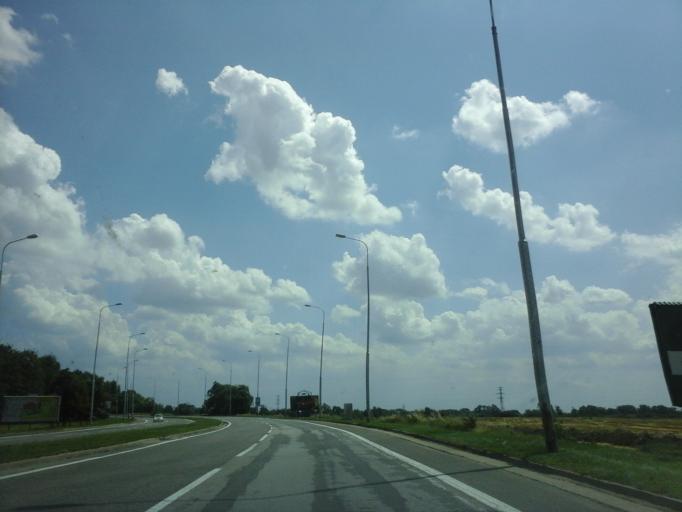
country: AT
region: Burgenland
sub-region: Politischer Bezirk Neusiedl am See
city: Kittsee
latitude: 48.0967
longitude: 17.1012
